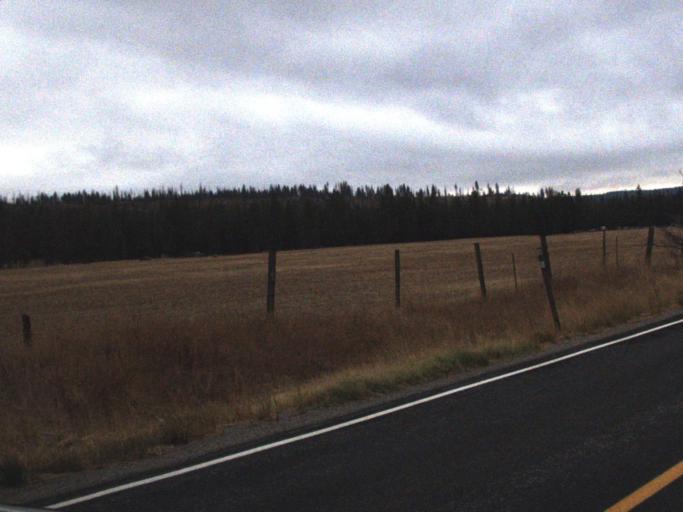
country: US
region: Washington
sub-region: Spokane County
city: Fairchild Air Force Base
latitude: 47.8693
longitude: -117.8405
